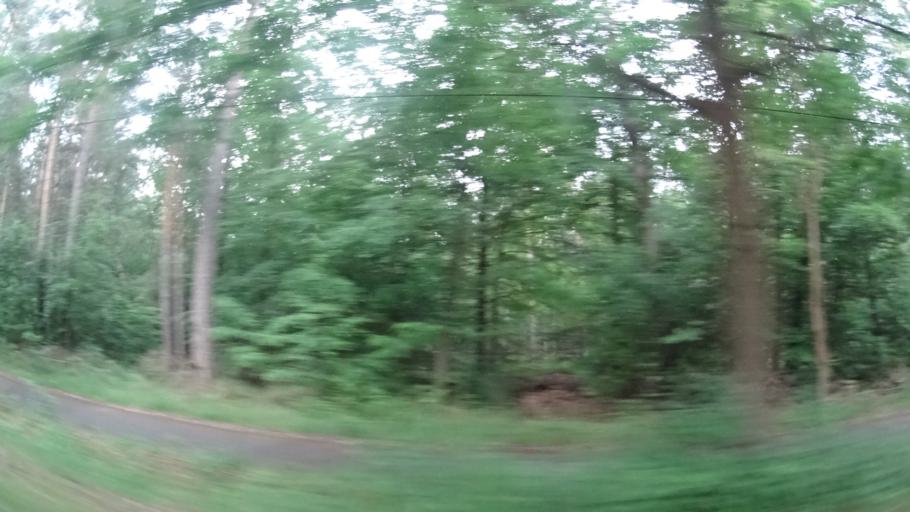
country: DE
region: Rheinland-Pfalz
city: Dudenhofen
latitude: 49.3476
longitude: 8.3819
